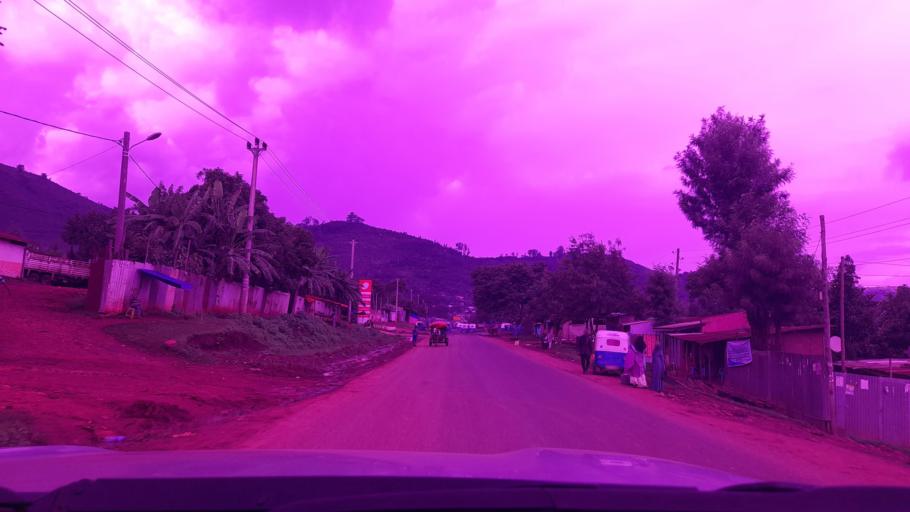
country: ET
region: Oromiya
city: Jima
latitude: 7.6694
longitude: 36.8624
